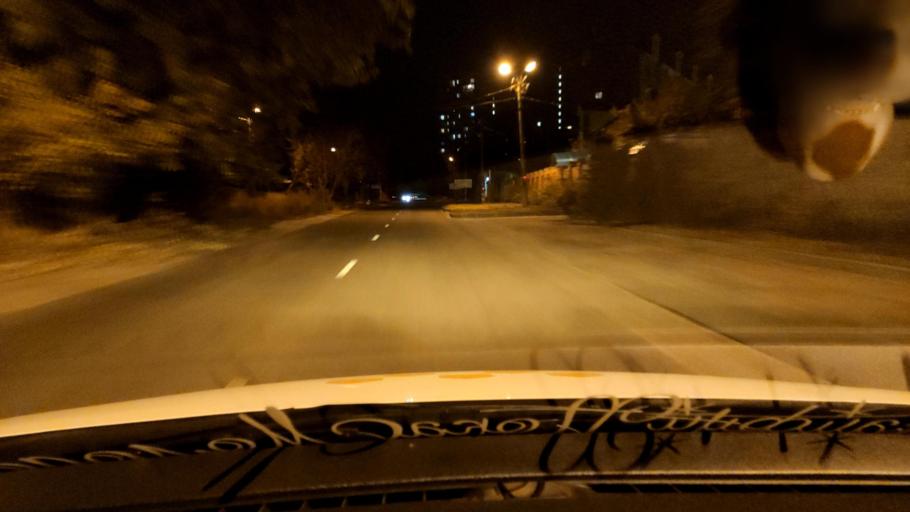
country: RU
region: Voronezj
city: Voronezh
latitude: 51.7010
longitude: 39.2006
